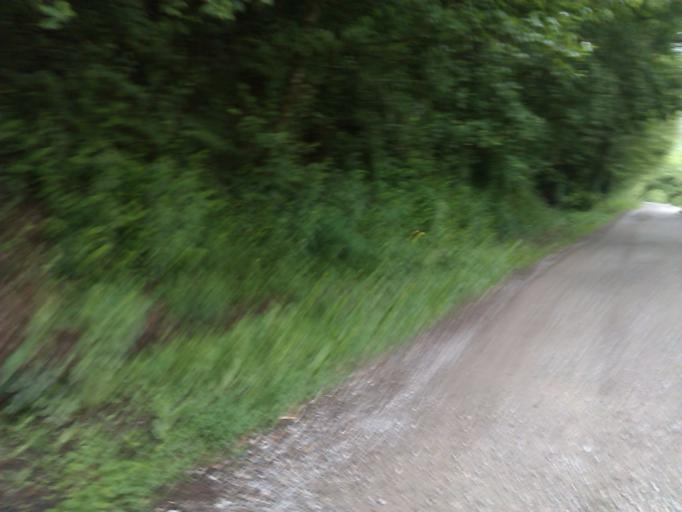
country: ES
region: Basque Country
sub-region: Provincia de Guipuzcoa
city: Andoain
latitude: 43.1966
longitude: -2.0100
